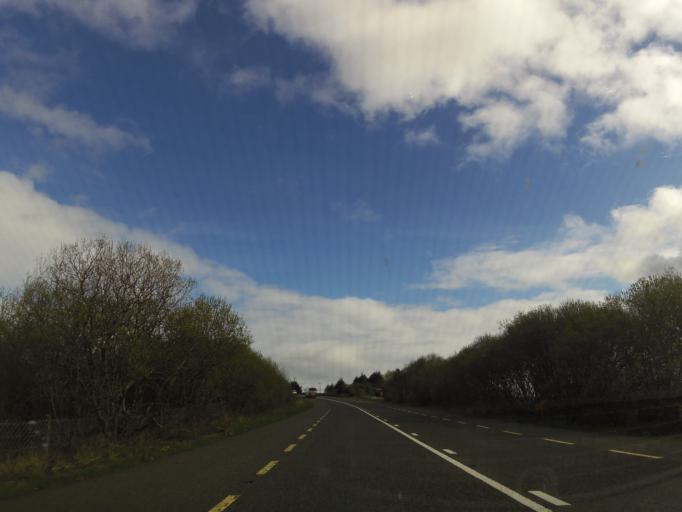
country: IE
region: Connaught
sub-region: Maigh Eo
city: Ballyhaunis
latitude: 53.9059
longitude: -8.7947
